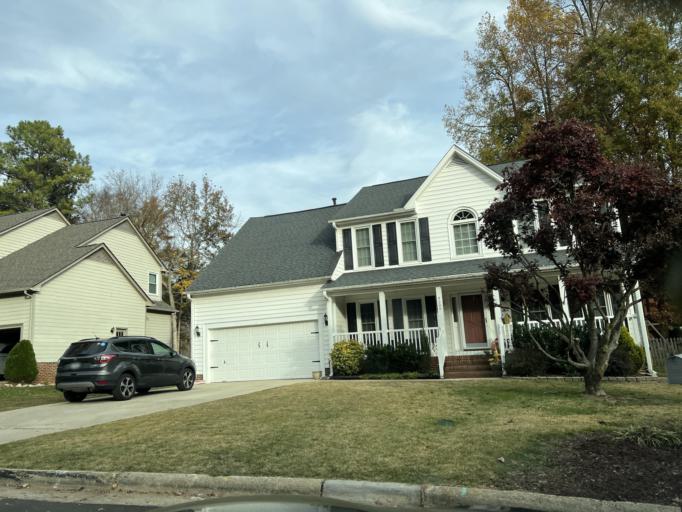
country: US
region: North Carolina
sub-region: Wake County
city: Wake Forest
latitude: 35.9014
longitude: -78.5840
